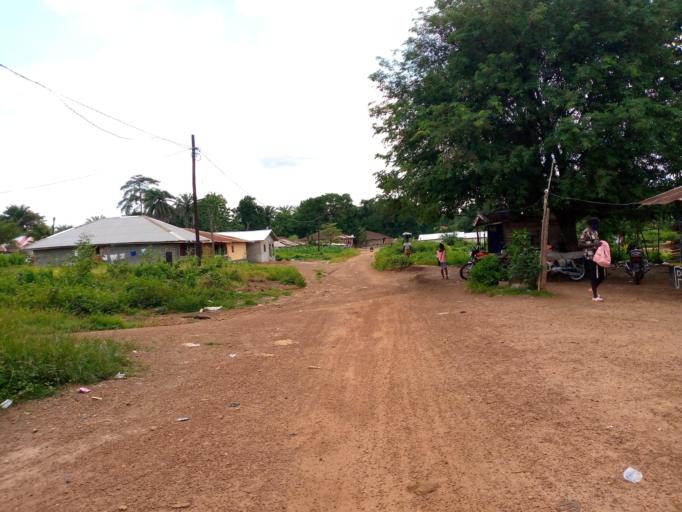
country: SL
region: Northern Province
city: Magburaka
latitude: 8.7105
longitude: -11.9324
